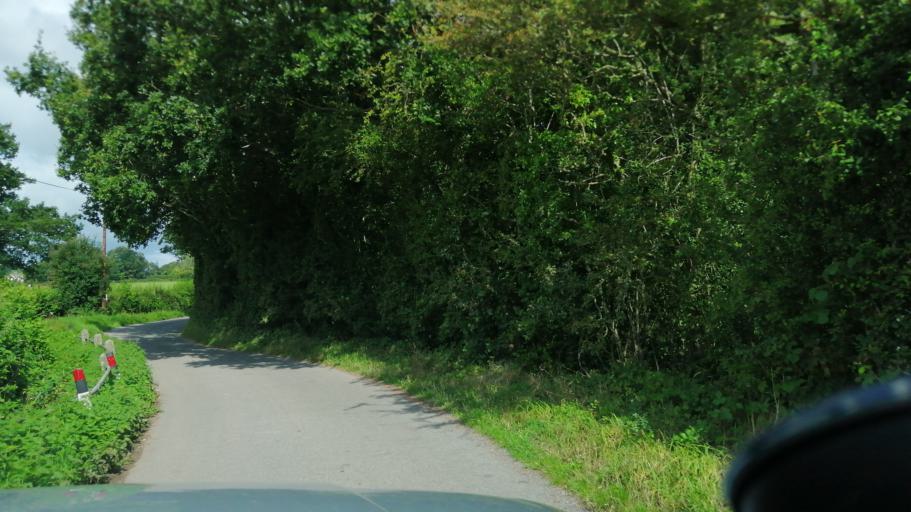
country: GB
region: England
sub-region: Herefordshire
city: Kinnersley
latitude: 52.1376
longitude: -2.9544
